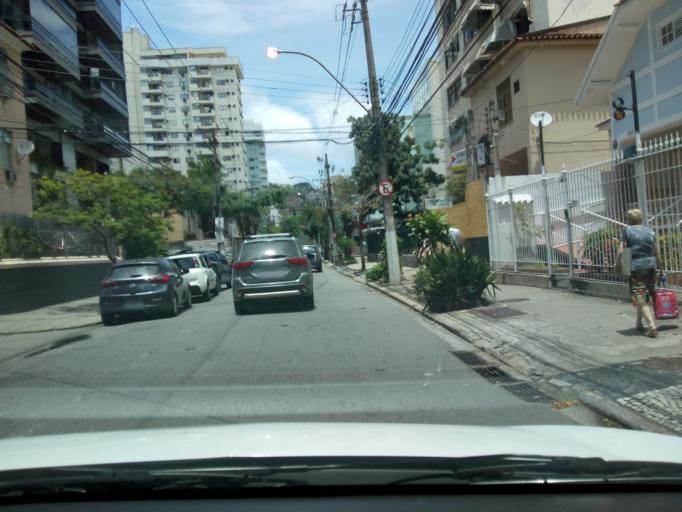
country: BR
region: Rio de Janeiro
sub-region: Niteroi
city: Niteroi
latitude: -22.9071
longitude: -43.1048
